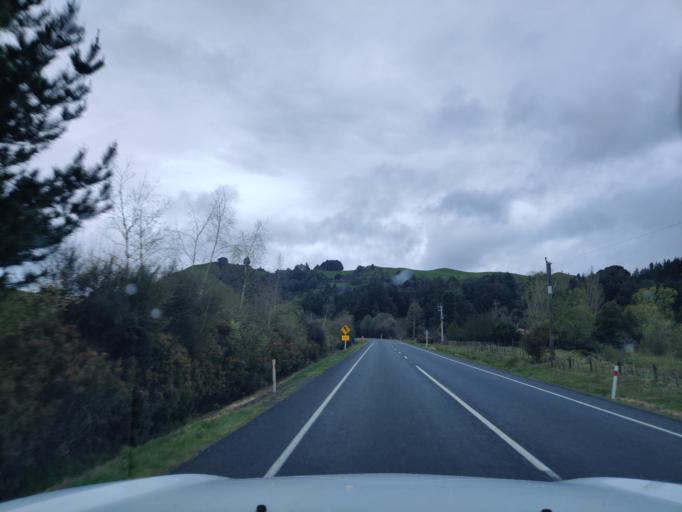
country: NZ
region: Waikato
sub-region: Otorohanga District
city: Otorohanga
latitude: -38.5753
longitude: 175.2137
